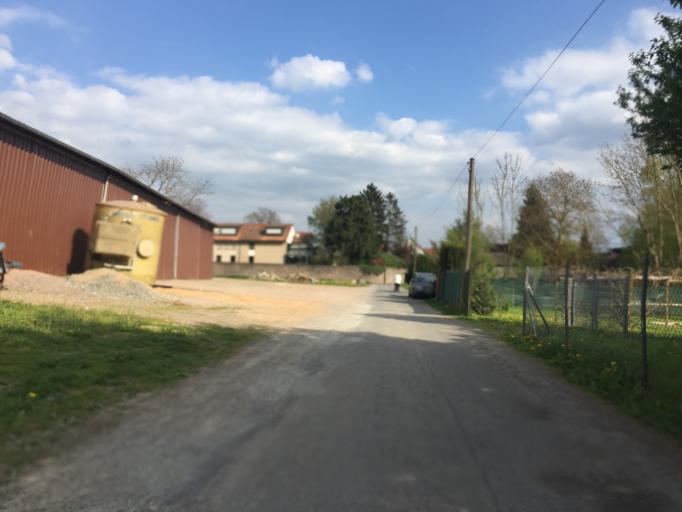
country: DE
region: Bavaria
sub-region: Regierungsbezirk Unterfranken
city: Glattbach
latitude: 49.9886
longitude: 9.1342
